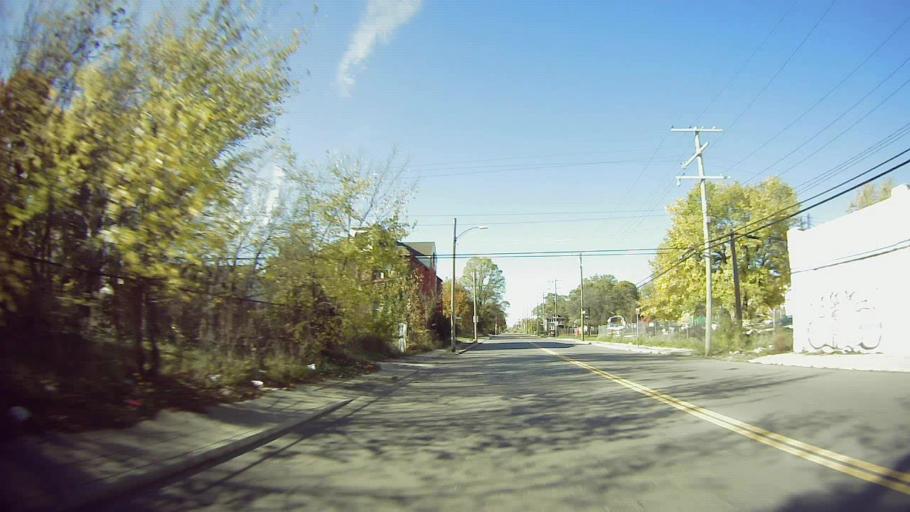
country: US
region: Michigan
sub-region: Wayne County
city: Dearborn
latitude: 42.3884
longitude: -83.1640
